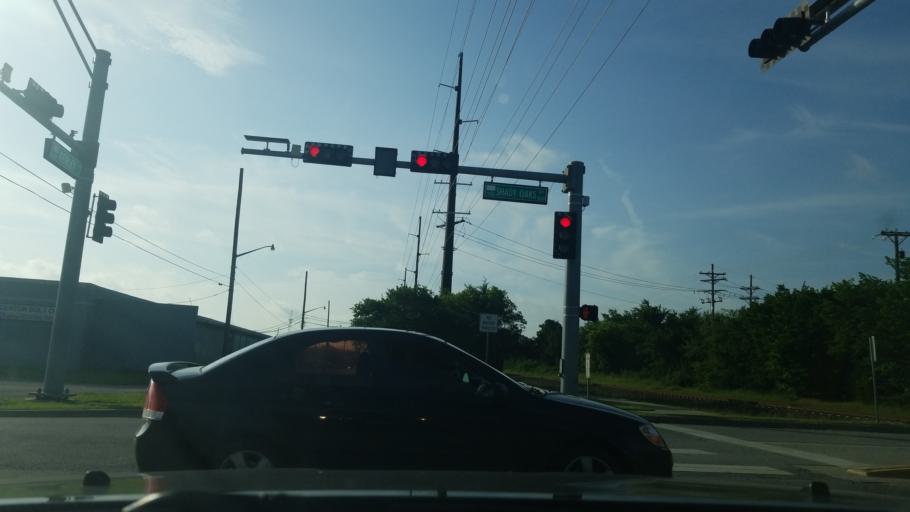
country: US
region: Texas
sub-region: Denton County
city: Denton
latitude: 33.2016
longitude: -97.1160
